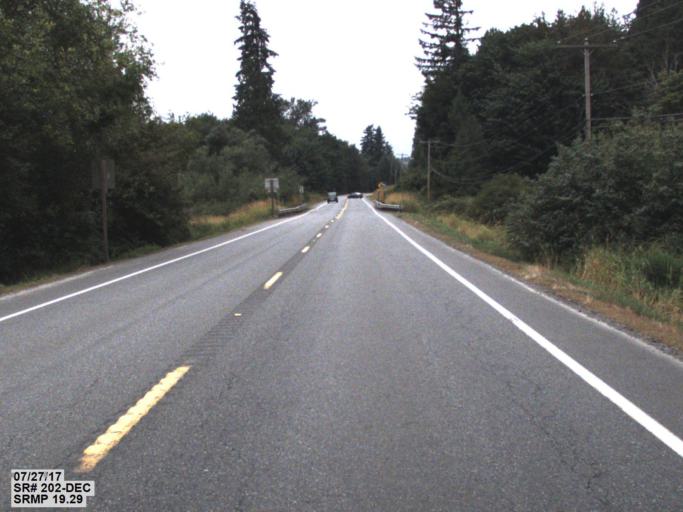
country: US
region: Washington
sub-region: King County
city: Fall City
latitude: 47.5794
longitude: -121.9352
